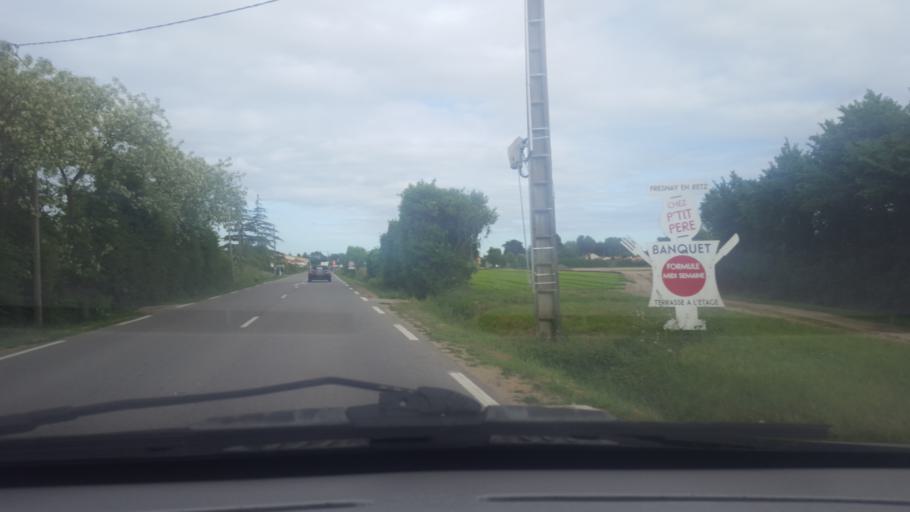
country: FR
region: Pays de la Loire
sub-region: Departement de la Loire-Atlantique
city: Bourgneuf-en-Retz
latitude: 47.0270
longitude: -1.8841
